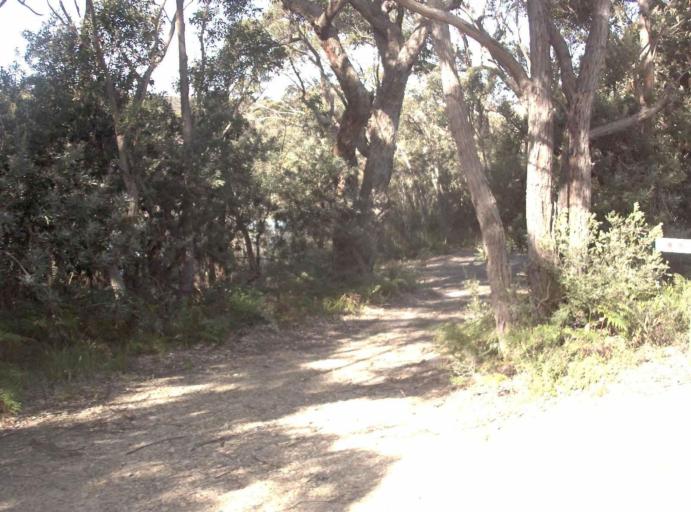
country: AU
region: Victoria
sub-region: East Gippsland
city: Lakes Entrance
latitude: -37.7982
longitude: 148.6829
